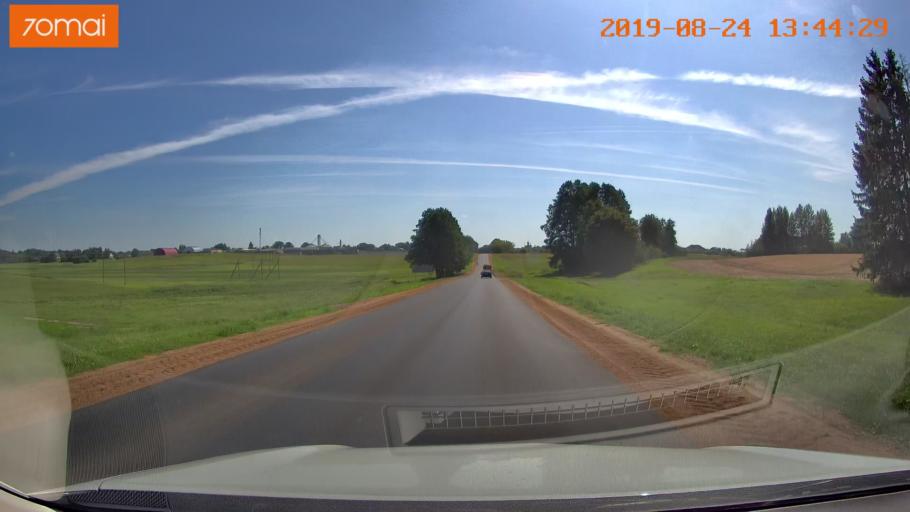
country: BY
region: Minsk
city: Samakhvalavichy
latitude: 53.6886
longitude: 27.5248
